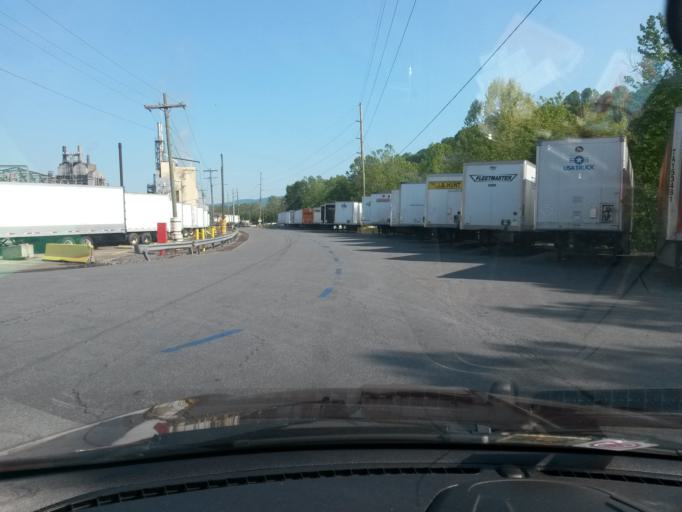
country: US
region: Virginia
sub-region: Rockbridge County
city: Glasgow
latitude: 37.5310
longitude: -79.3535
